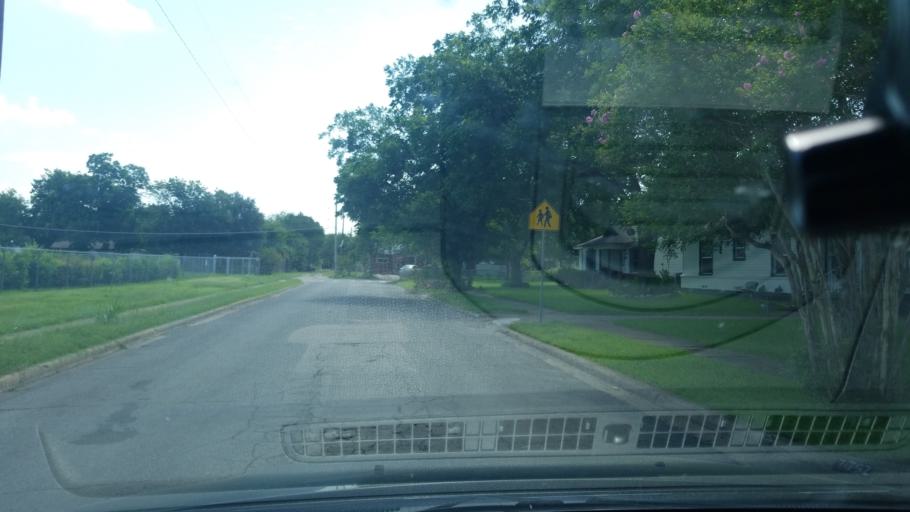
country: US
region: Texas
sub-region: Dallas County
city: Balch Springs
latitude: 32.7415
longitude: -96.6881
